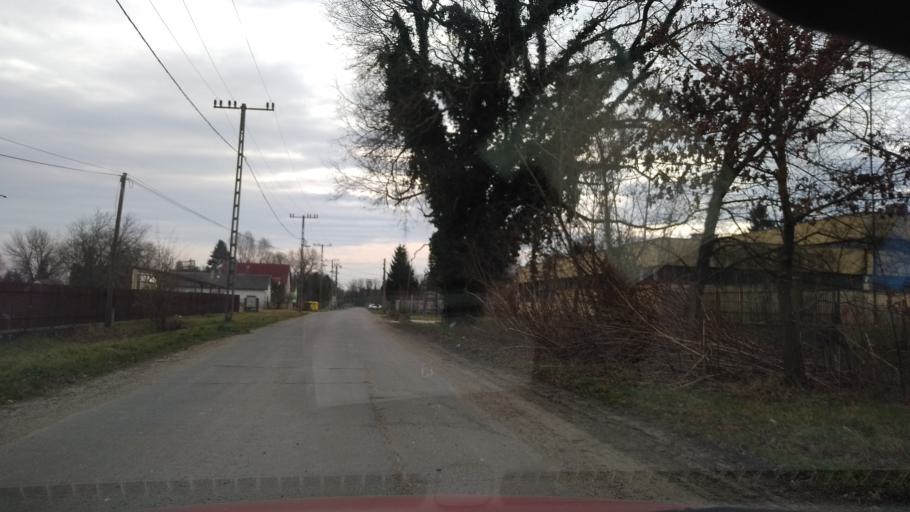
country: HU
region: Somogy
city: Barcs
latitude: 45.9563
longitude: 17.4413
